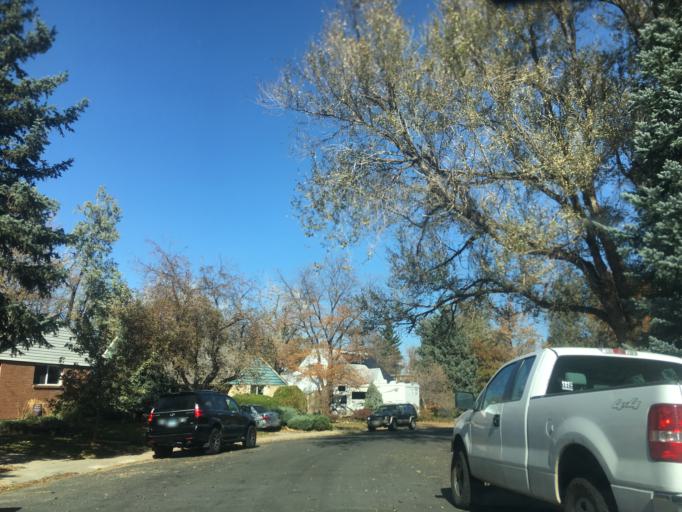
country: US
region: Colorado
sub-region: Boulder County
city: Boulder
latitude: 39.9869
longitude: -105.2426
